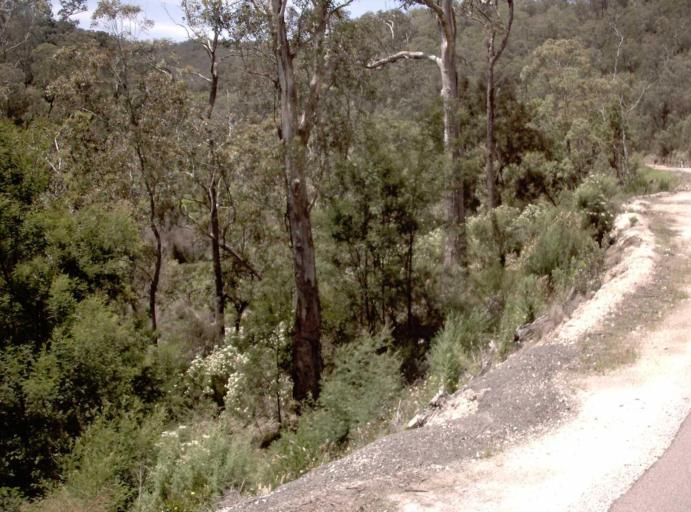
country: AU
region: Victoria
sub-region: East Gippsland
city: Lakes Entrance
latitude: -37.5342
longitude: 147.8545
